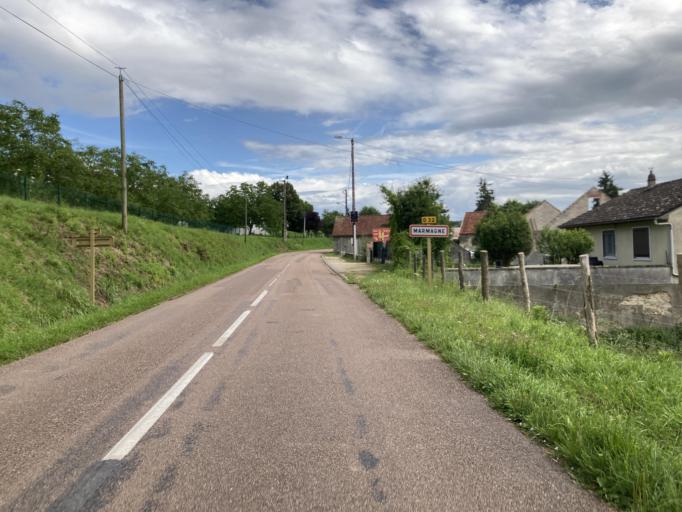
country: FR
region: Bourgogne
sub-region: Departement de la Cote-d'Or
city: Montbard
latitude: 47.6258
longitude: 4.3682
